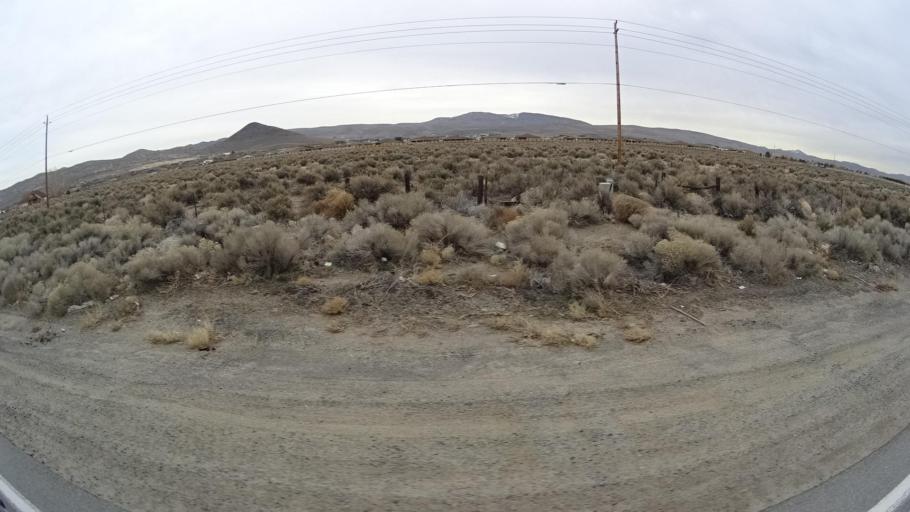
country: US
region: Nevada
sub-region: Washoe County
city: Spanish Springs
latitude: 39.6688
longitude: -119.7031
